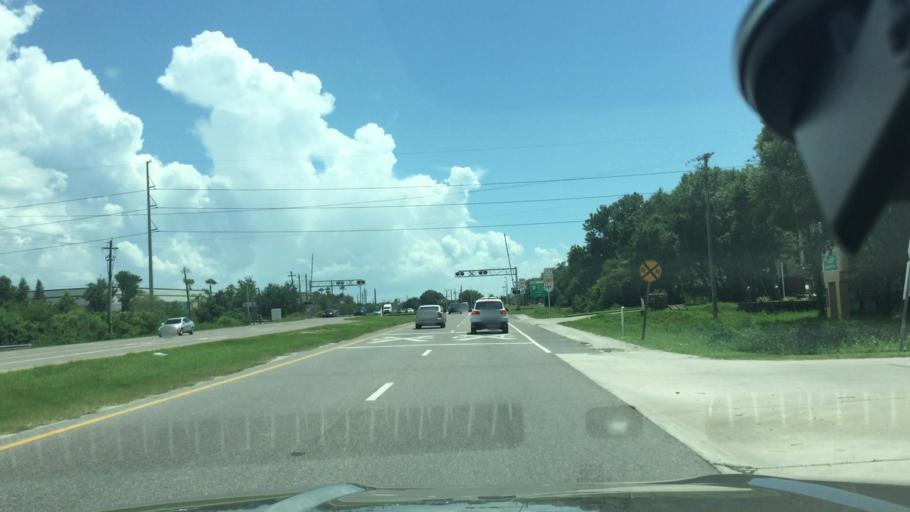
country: US
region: Florida
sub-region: Hillsborough County
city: Carrollwood Village
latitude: 28.0392
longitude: -82.5420
